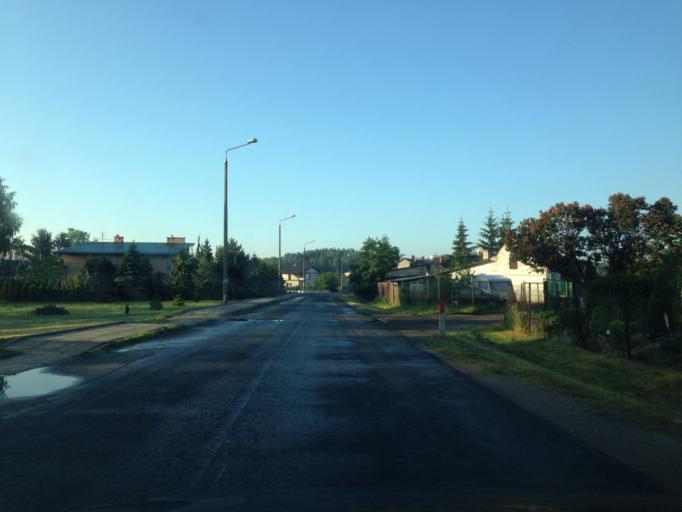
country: PL
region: Pomeranian Voivodeship
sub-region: Powiat tczewski
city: Gniew
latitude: 53.8241
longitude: 18.8161
